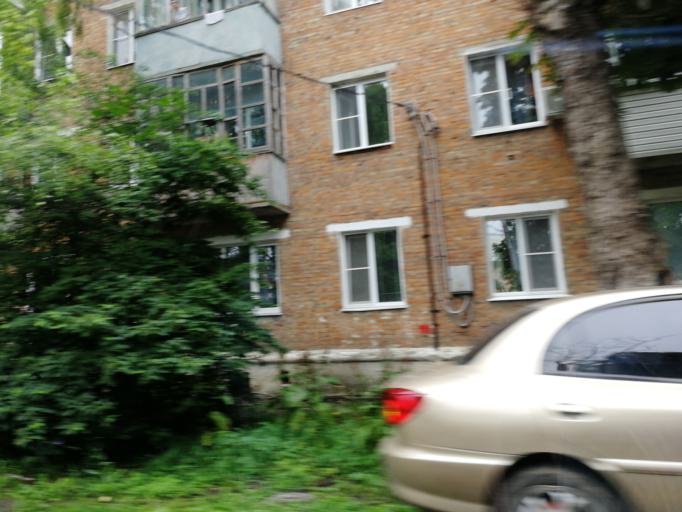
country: RU
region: Tula
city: Bogoroditsk
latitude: 53.7691
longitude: 38.1262
